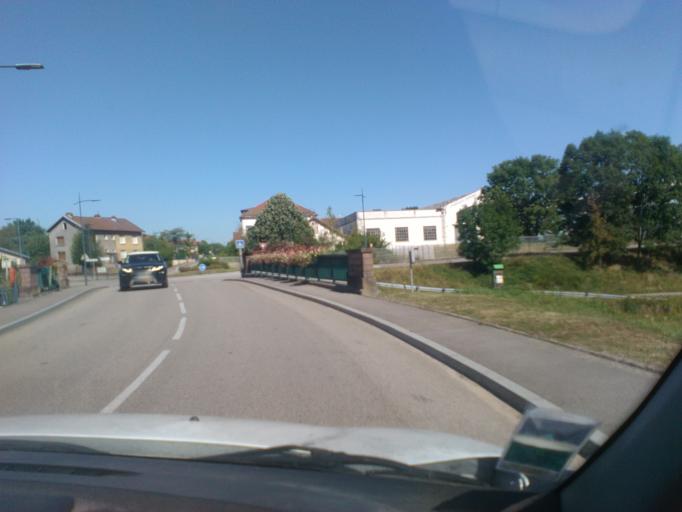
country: FR
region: Lorraine
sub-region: Departement des Vosges
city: Golbey
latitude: 48.2012
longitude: 6.4288
